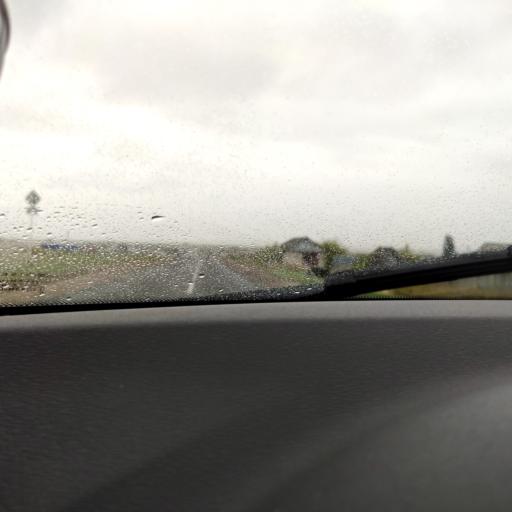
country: RU
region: Samara
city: Yelkhovka
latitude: 53.7445
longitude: 50.2533
